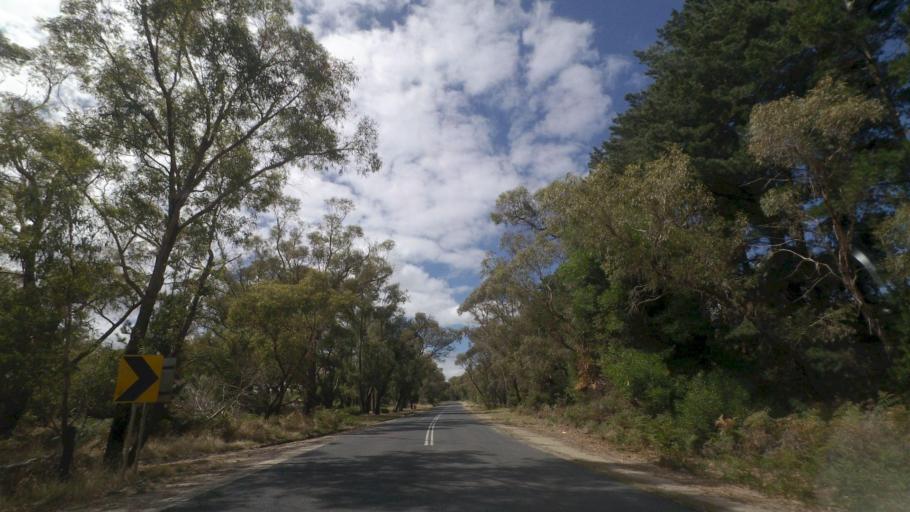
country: AU
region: Victoria
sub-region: Cardinia
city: Koo-Wee-Rup
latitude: -38.2903
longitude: 145.6225
